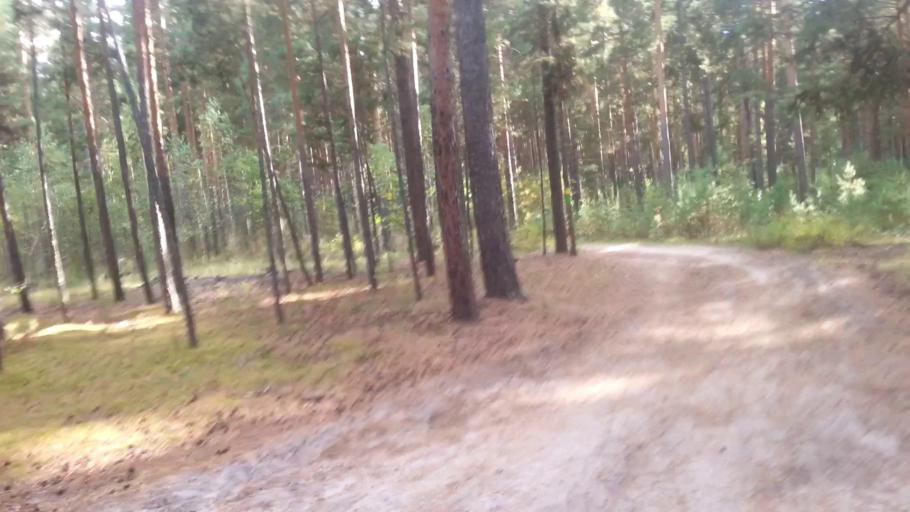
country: RU
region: Altai Krai
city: Yuzhnyy
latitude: 53.2848
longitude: 83.6991
